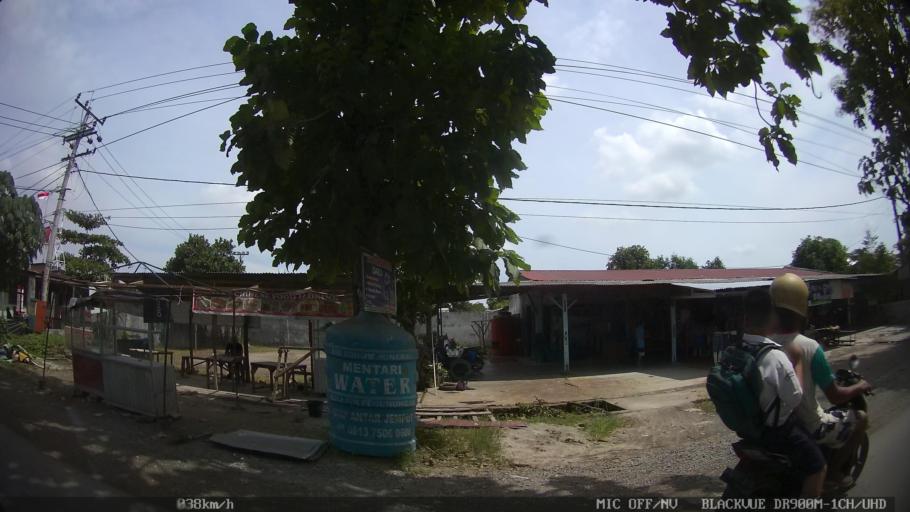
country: ID
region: North Sumatra
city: Medan
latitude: 3.6509
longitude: 98.7059
